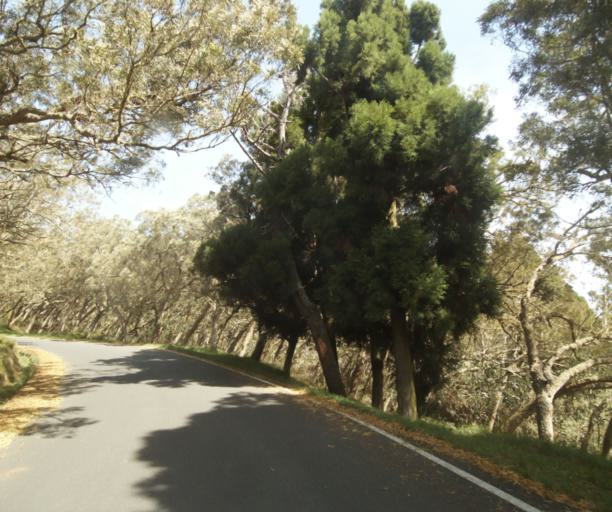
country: RE
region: Reunion
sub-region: Reunion
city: Trois-Bassins
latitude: -21.0598
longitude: 55.3703
